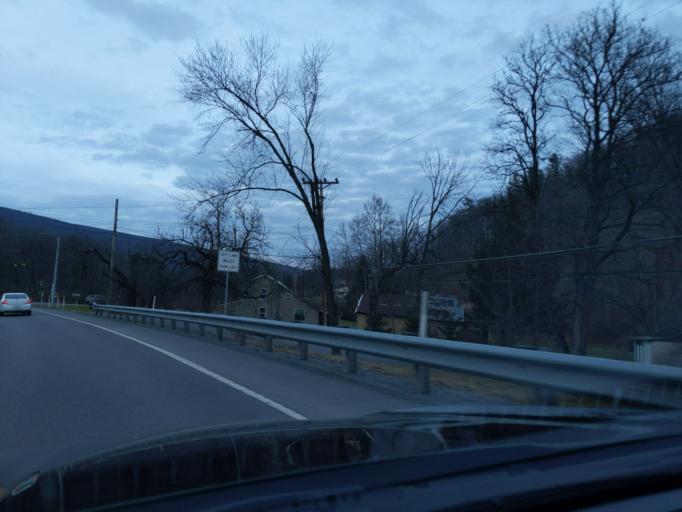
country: US
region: Pennsylvania
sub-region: Blair County
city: Lakemont
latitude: 40.4512
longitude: -78.3524
